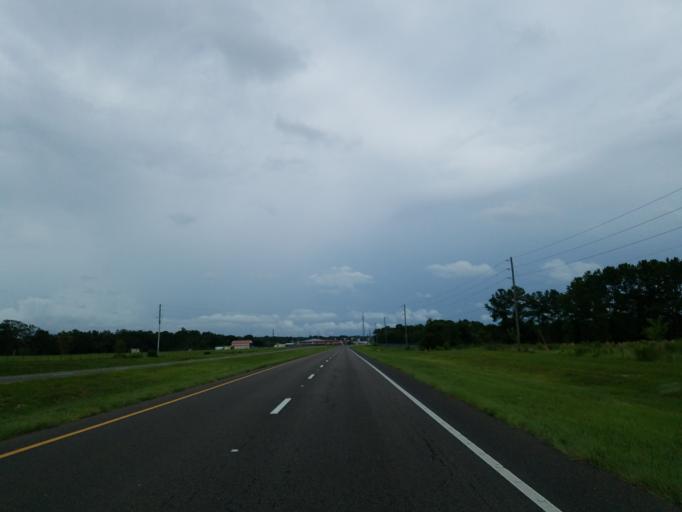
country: US
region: Florida
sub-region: Sumter County
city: Wildwood
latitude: 28.8767
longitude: -82.1048
